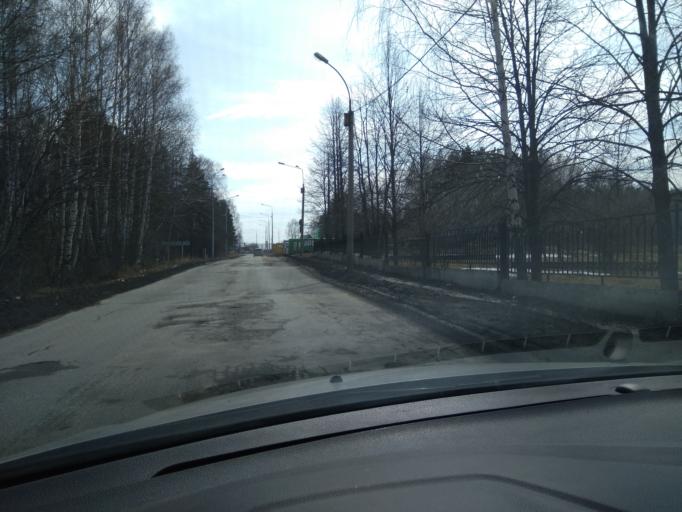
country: RU
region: Sverdlovsk
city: Shuvakish
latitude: 56.8944
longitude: 60.4852
